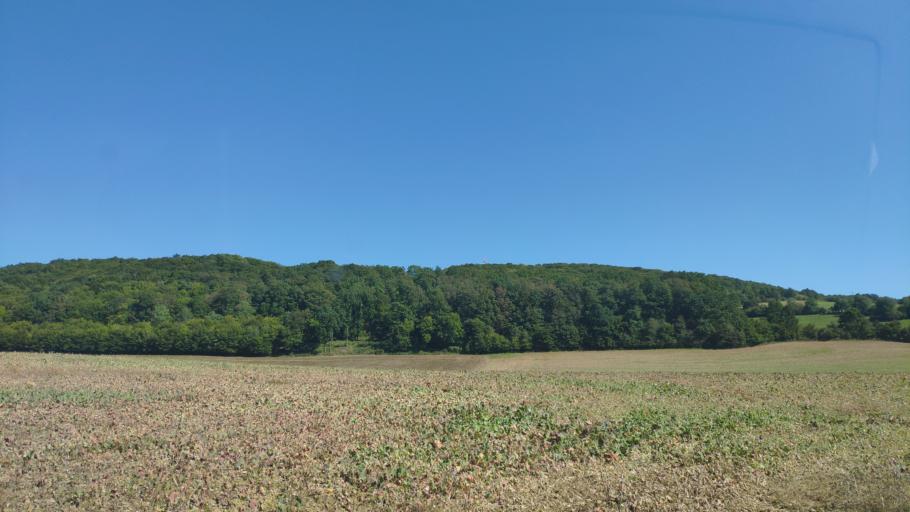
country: SK
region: Presovsky
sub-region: Okres Presov
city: Presov
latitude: 48.9660
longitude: 21.1392
